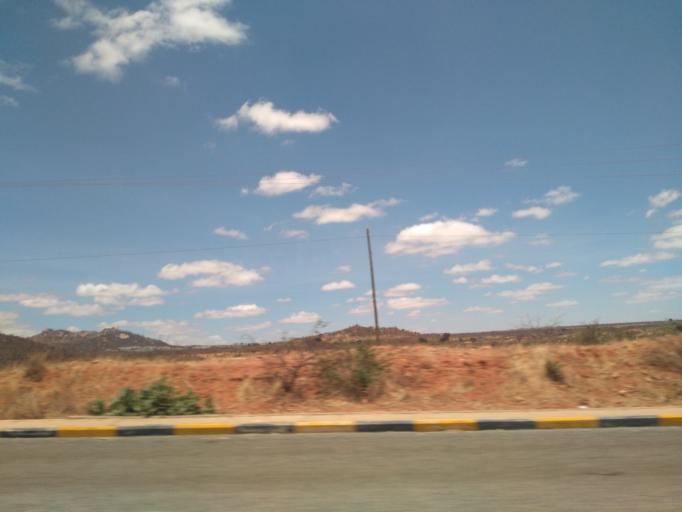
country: TZ
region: Dodoma
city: Kisasa
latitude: -6.2033
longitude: 35.8245
